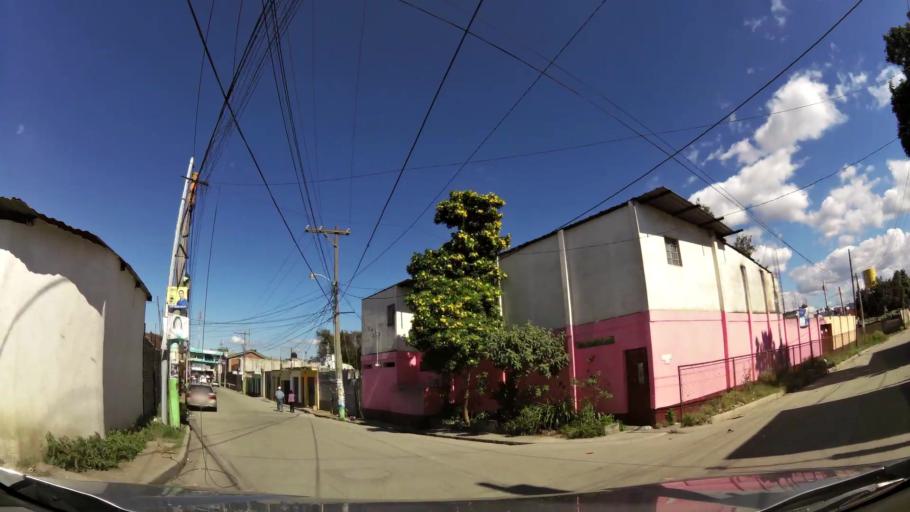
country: GT
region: Guatemala
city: Petapa
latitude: 14.5031
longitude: -90.5668
